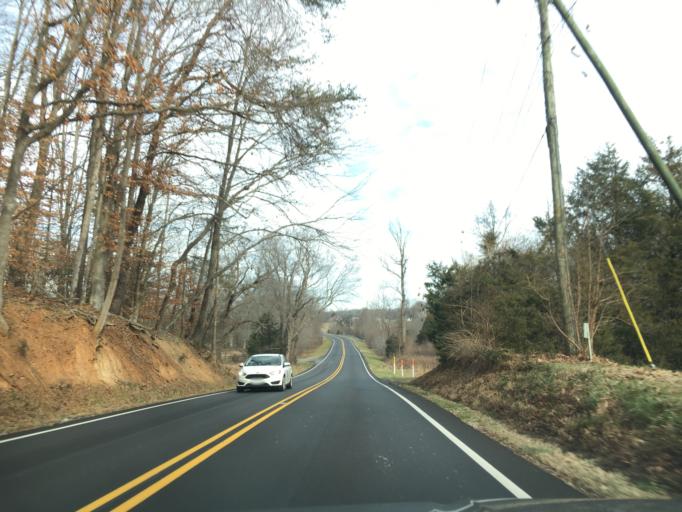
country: US
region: Virginia
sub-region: Goochland County
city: Goochland
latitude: 37.7909
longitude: -77.8735
